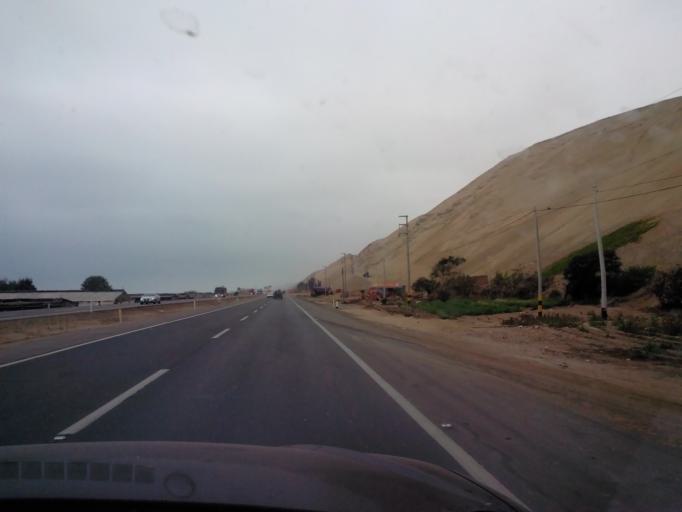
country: PE
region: Ica
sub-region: Provincia de Chincha
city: San Pedro
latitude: -13.3407
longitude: -76.2304
